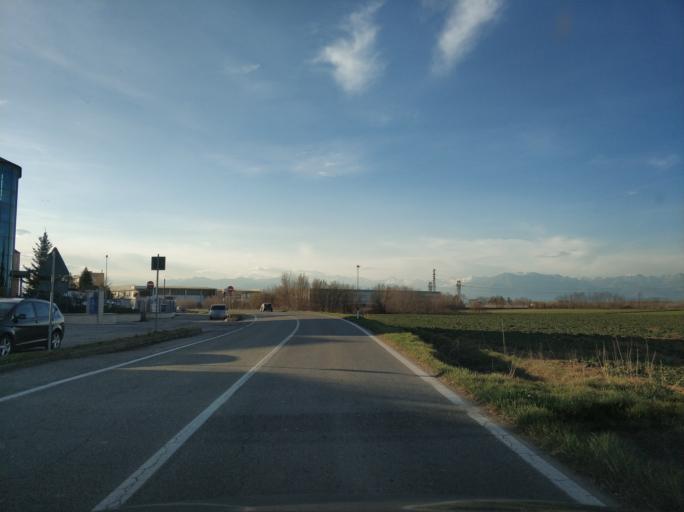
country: IT
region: Piedmont
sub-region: Provincia di Torino
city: Volpiano
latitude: 45.1931
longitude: 7.8004
